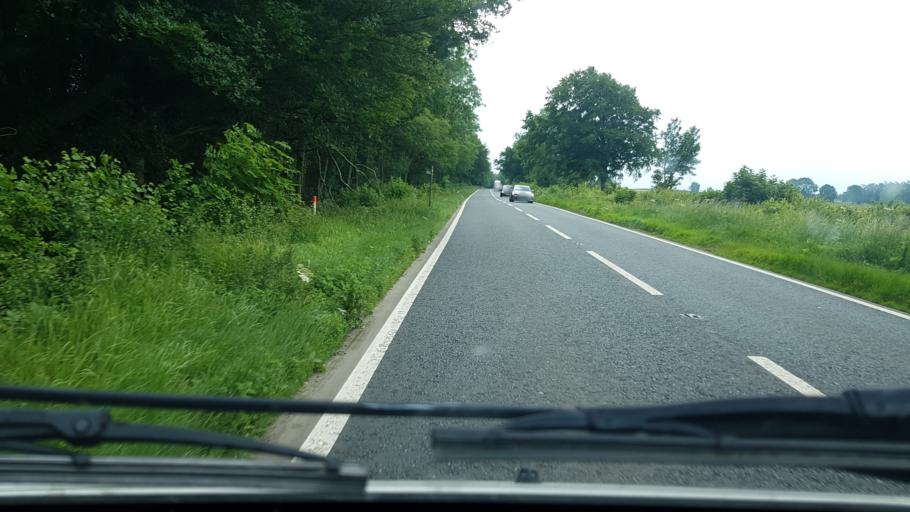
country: GB
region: England
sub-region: Gloucestershire
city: Chipping Campden
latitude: 52.0028
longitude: -1.7868
